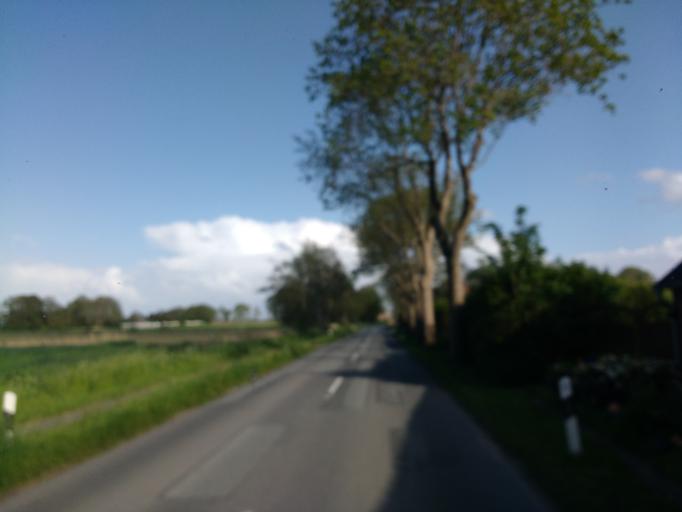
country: DE
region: Lower Saxony
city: Schillig
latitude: 53.7015
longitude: 7.9944
